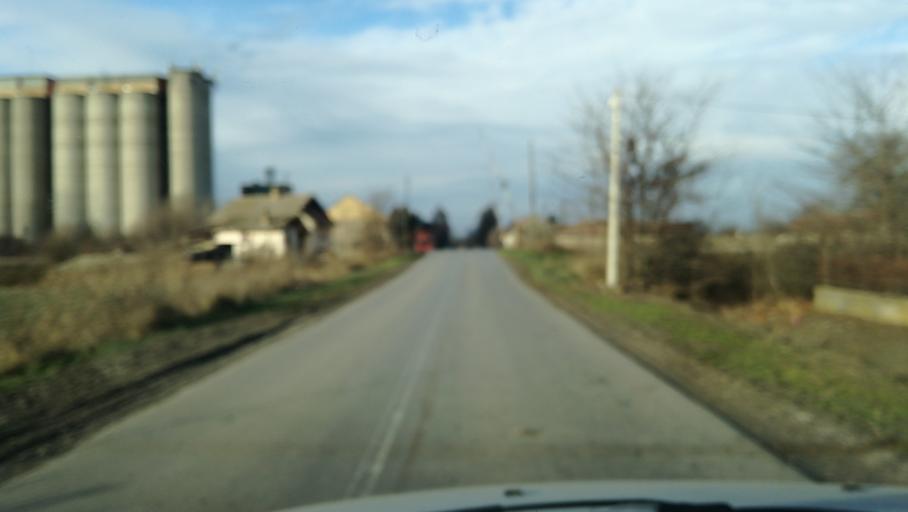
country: RS
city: Banatsko Veliko Selo
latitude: 45.8087
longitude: 20.6129
